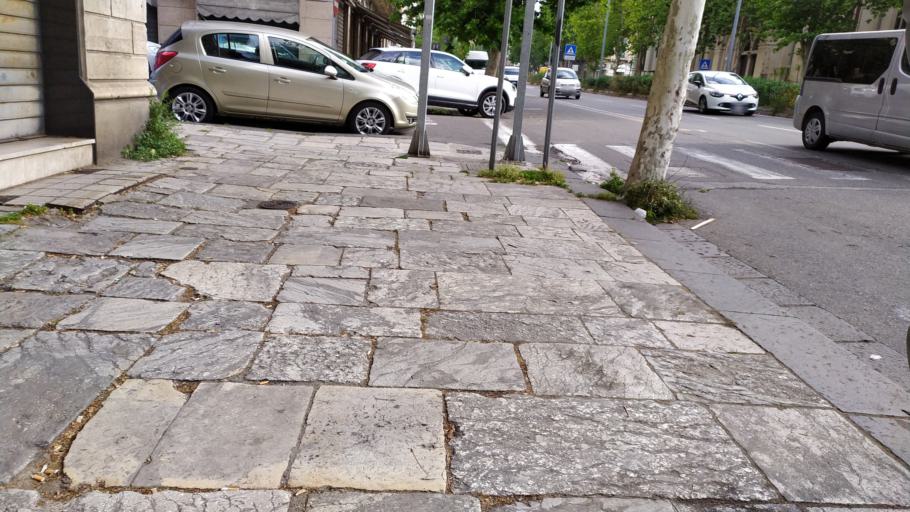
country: IT
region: Sicily
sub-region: Messina
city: Messina
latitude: 38.2005
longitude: 15.5573
